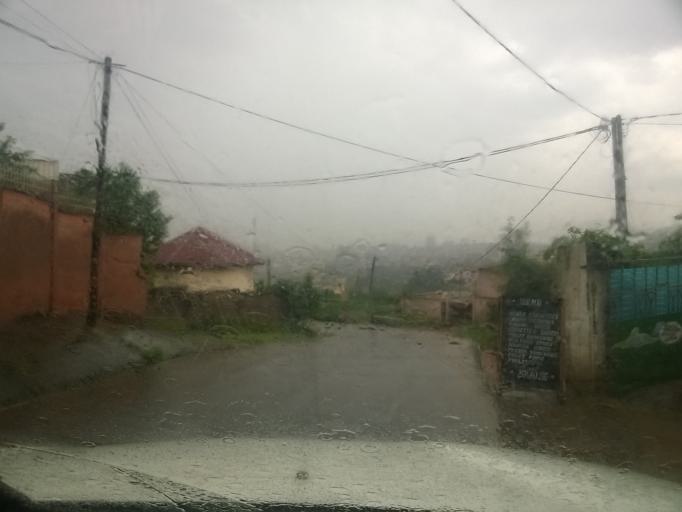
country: CM
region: Centre
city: Yaounde
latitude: 3.8724
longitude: 11.5344
